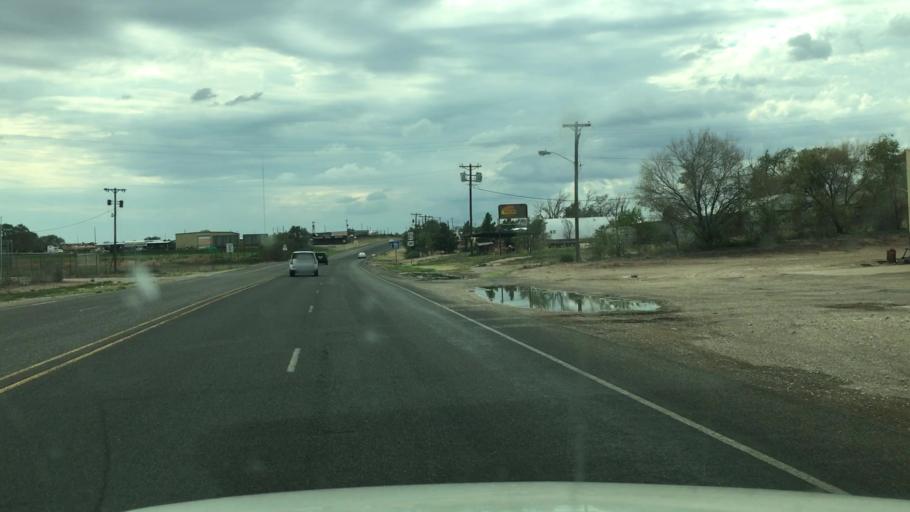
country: US
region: Texas
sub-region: Terry County
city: Brownfield
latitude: 33.1792
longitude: -102.2919
